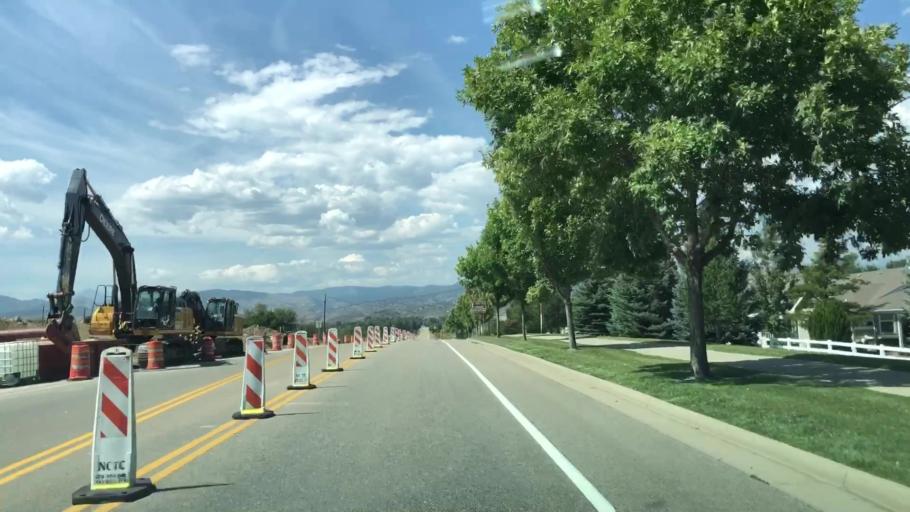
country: US
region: Colorado
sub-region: Larimer County
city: Loveland
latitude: 40.3929
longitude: -105.1379
